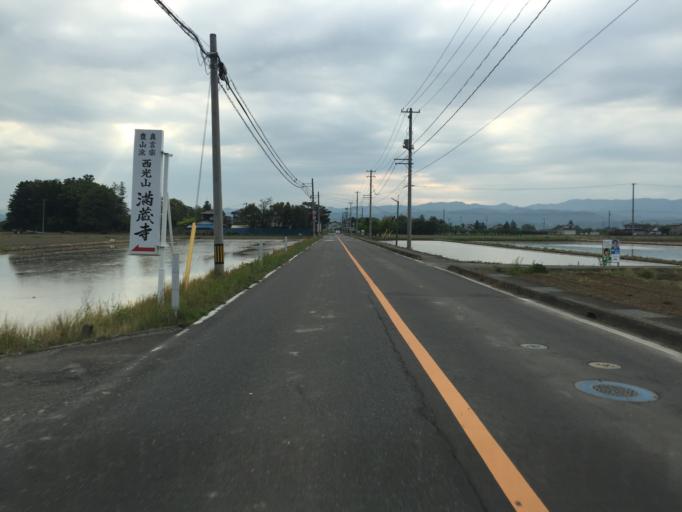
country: JP
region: Fukushima
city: Hobaramachi
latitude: 37.8501
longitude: 140.5463
